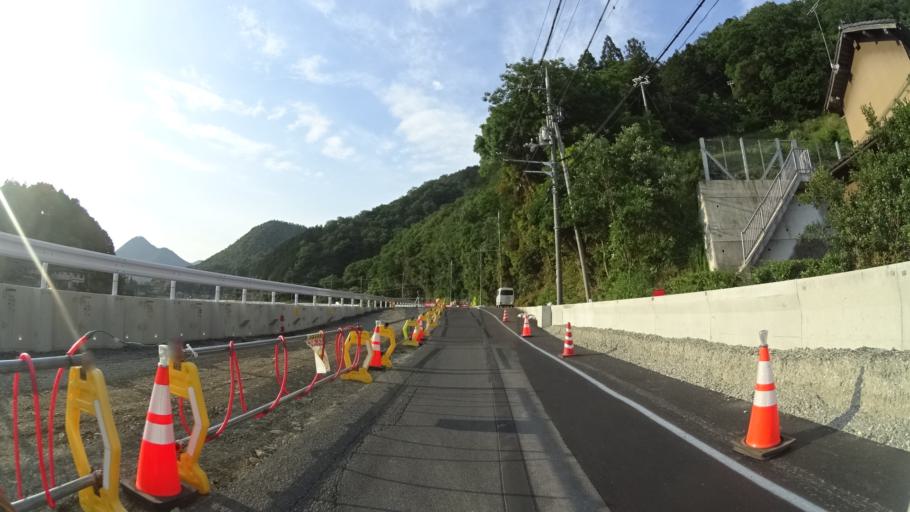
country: JP
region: Kyoto
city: Miyazu
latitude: 35.4267
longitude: 135.2155
